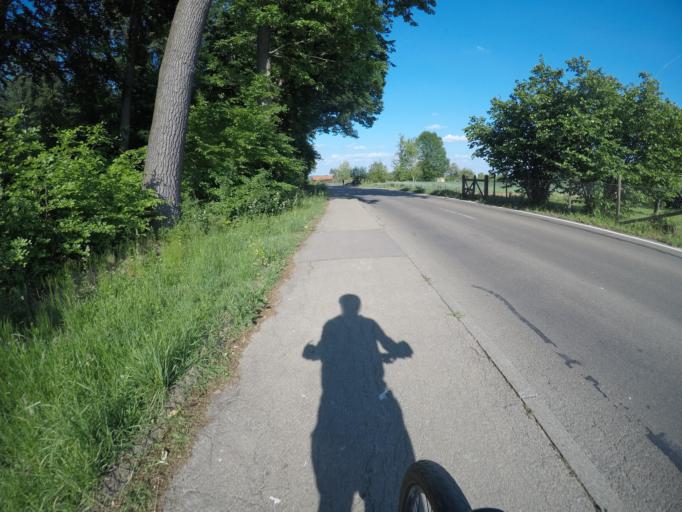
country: DE
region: Baden-Wuerttemberg
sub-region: Regierungsbezirk Stuttgart
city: Ostfildern
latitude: 48.7373
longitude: 9.2424
